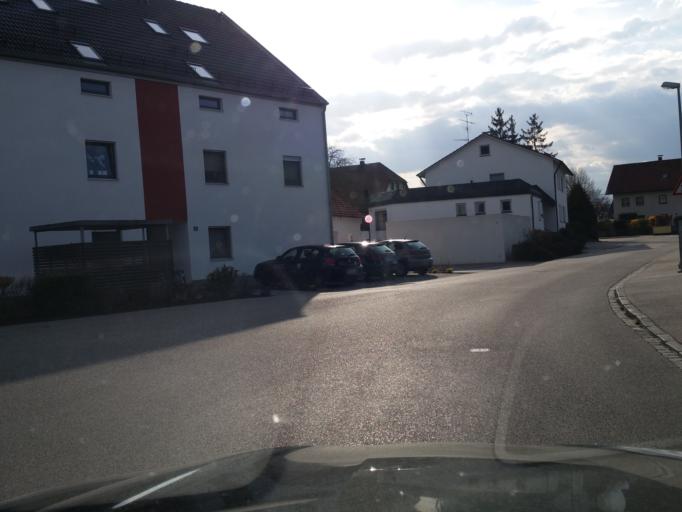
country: DE
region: Bavaria
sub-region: Lower Bavaria
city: Landshut
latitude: 48.5519
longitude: 12.1657
